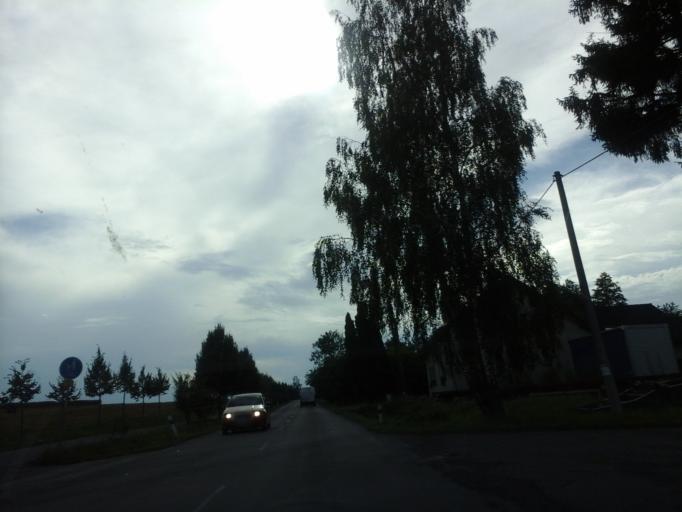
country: CZ
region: Pardubicky
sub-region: Okres Usti nad Orlici
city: Lanskroun
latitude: 49.9198
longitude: 16.6363
